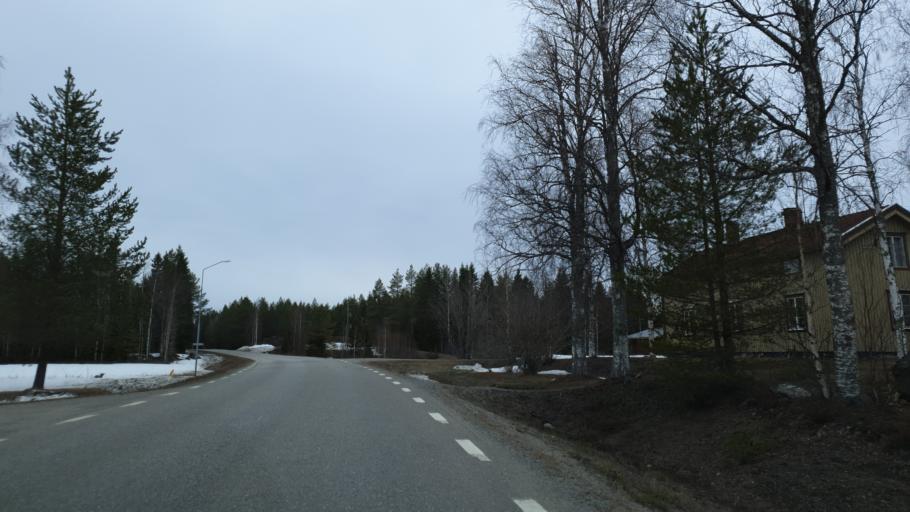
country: SE
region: Vaesterbotten
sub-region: Robertsfors Kommun
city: Robertsfors
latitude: 64.3915
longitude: 20.8955
